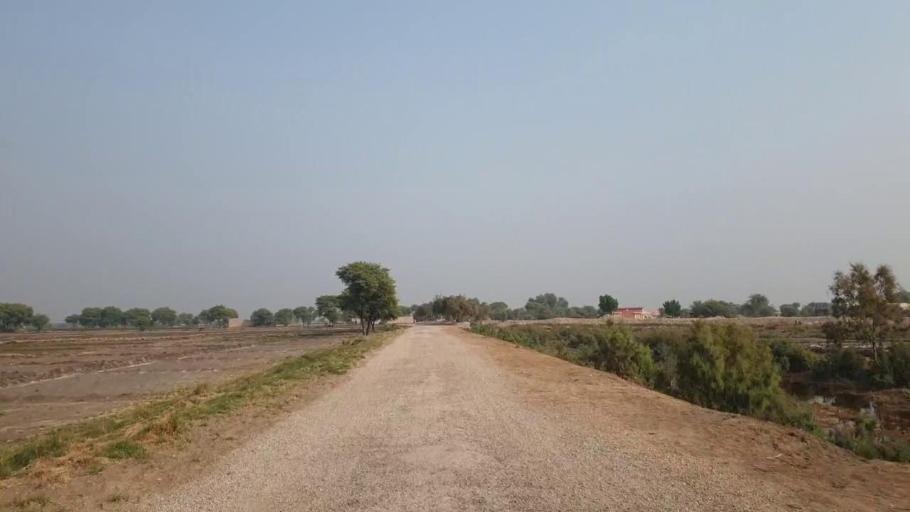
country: PK
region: Sindh
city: Bhan
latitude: 26.4584
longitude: 67.7259
